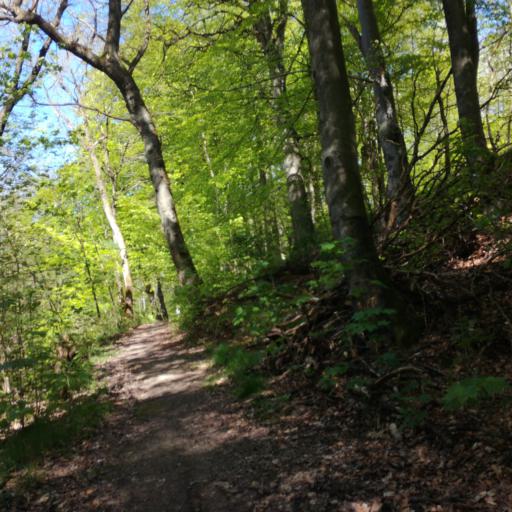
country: DK
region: South Denmark
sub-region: Vejle Kommune
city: Brejning
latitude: 55.6121
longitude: 9.6981
